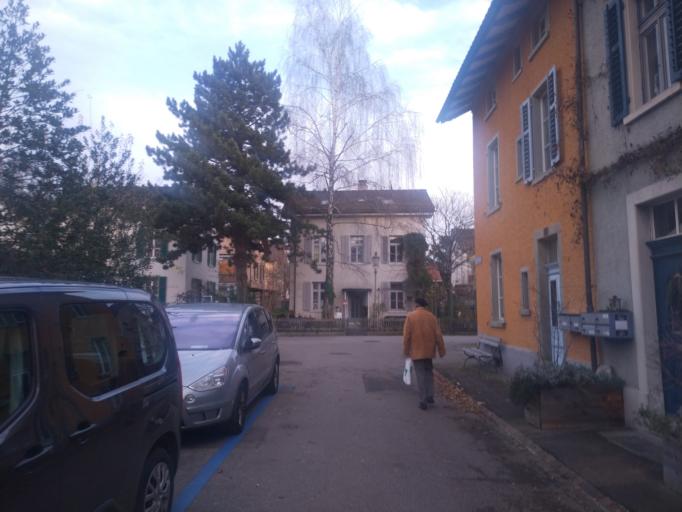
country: CH
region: Zurich
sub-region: Bezirk Winterthur
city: Mattenbach (Kreis 7) / Deutweg
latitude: 47.4966
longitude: 8.7395
